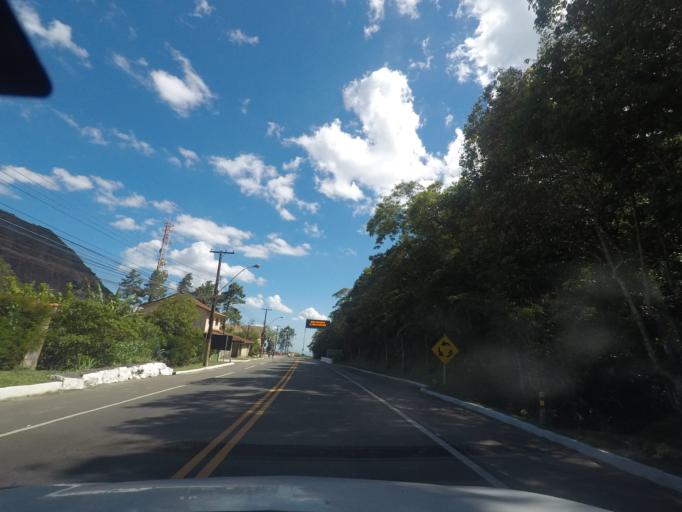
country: BR
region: Rio de Janeiro
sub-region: Teresopolis
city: Teresopolis
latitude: -22.4608
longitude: -42.9878
